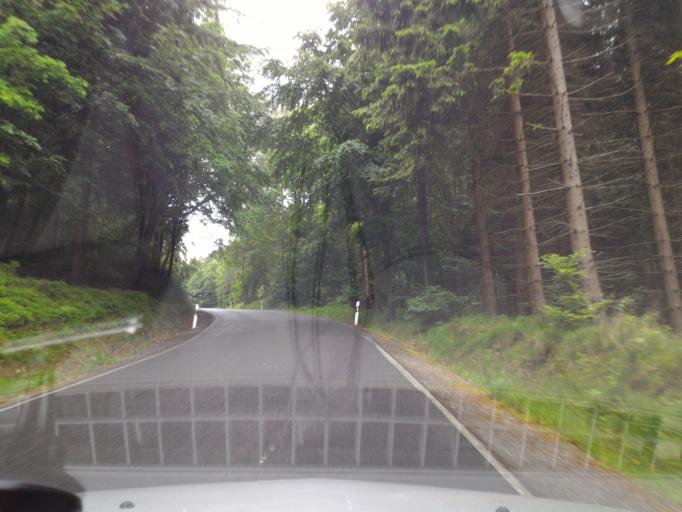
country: DE
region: Saxony
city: Kurort Oybin
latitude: 50.8309
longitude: 14.7415
